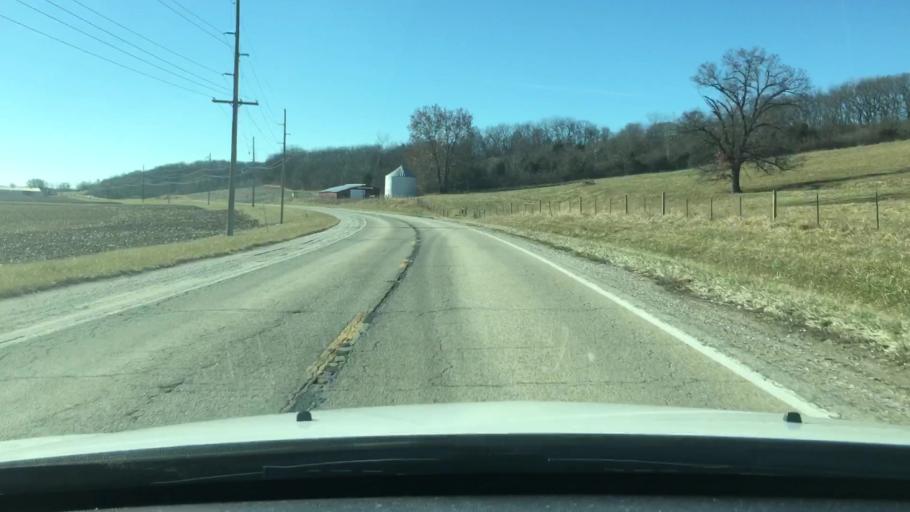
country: US
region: Illinois
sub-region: Fulton County
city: Astoria
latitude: 40.1741
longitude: -90.2858
